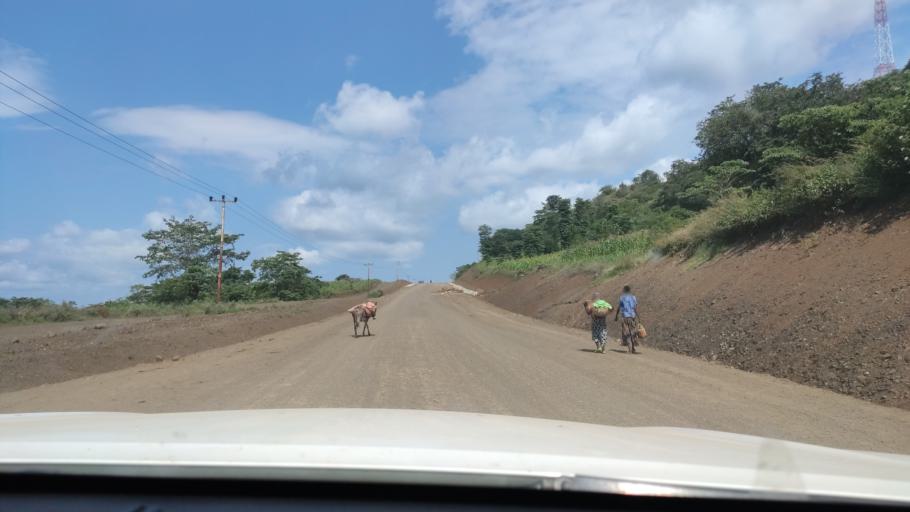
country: ET
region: Southern Nations, Nationalities, and People's Region
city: Felege Neway
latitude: 6.3937
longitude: 37.0726
